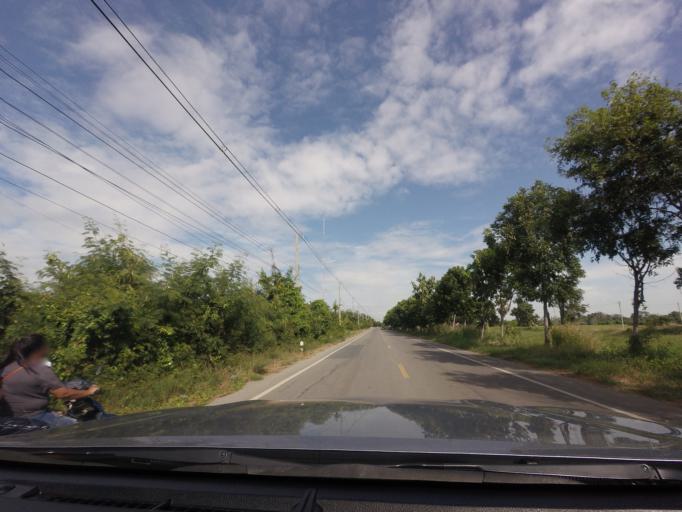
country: TH
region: Suphan Buri
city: Suphan Buri
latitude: 14.5362
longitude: 100.1147
